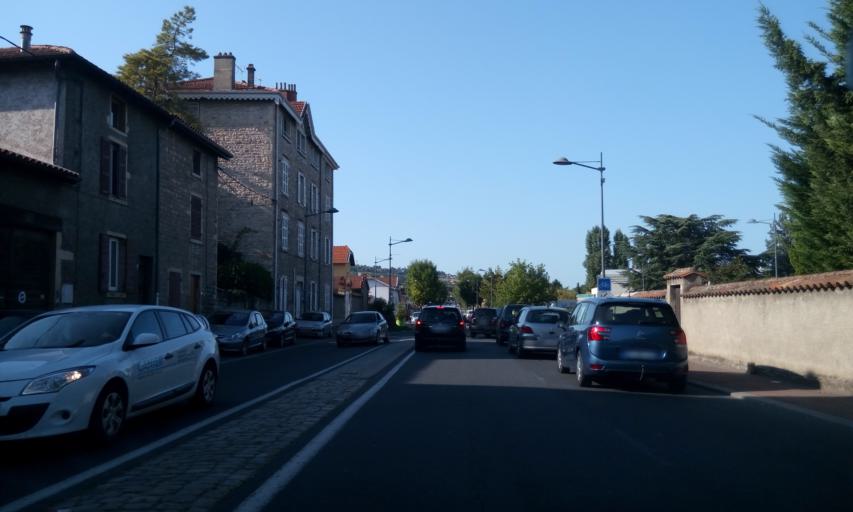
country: FR
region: Rhone-Alpes
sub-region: Departement du Rhone
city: Anse
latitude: 45.9396
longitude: 4.7166
